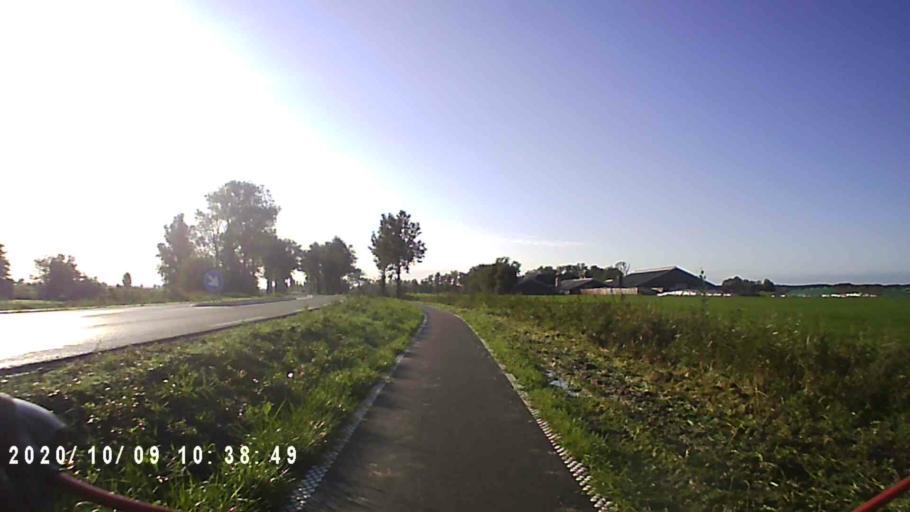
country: NL
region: Groningen
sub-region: Gemeente Winsum
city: Winsum
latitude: 53.2870
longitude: 6.5332
